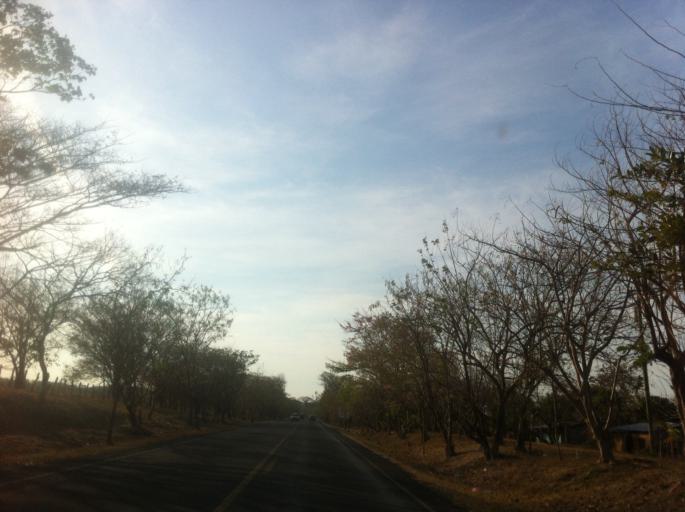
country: NI
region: Rivas
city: Cardenas
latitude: 11.2559
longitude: -85.6354
